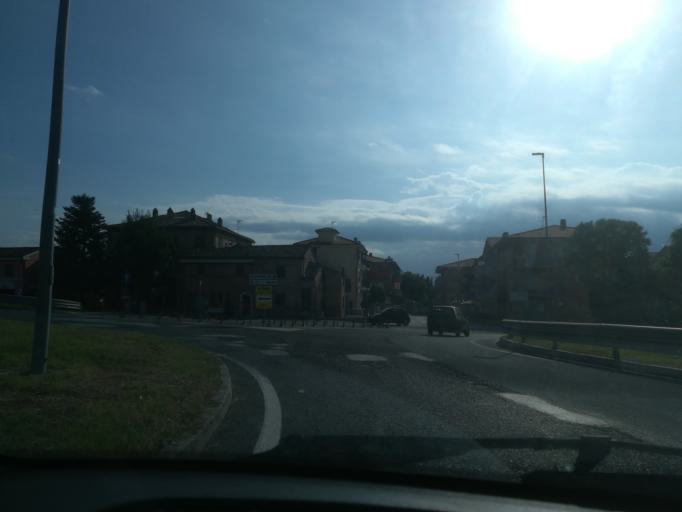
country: IT
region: The Marches
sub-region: Provincia di Macerata
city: Villa Potenza
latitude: 43.3207
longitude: 13.4279
